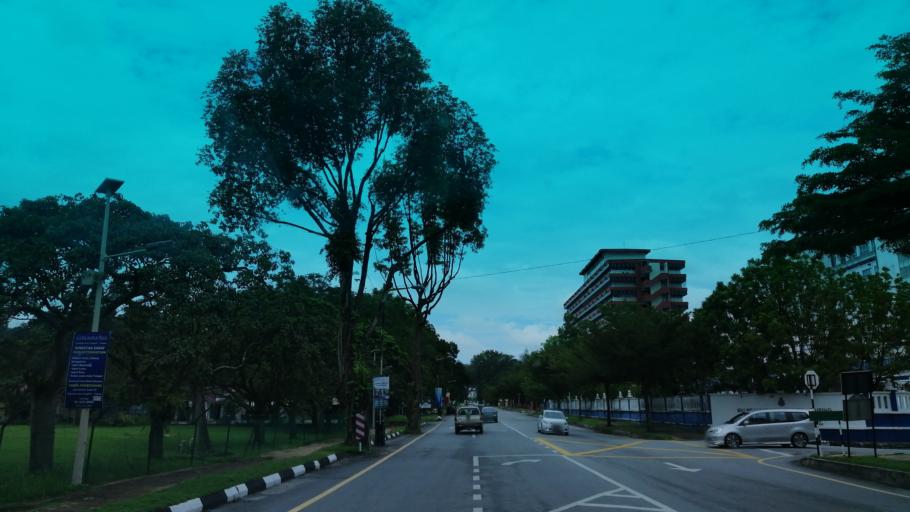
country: MY
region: Perak
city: Taiping
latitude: 4.8553
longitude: 100.7405
